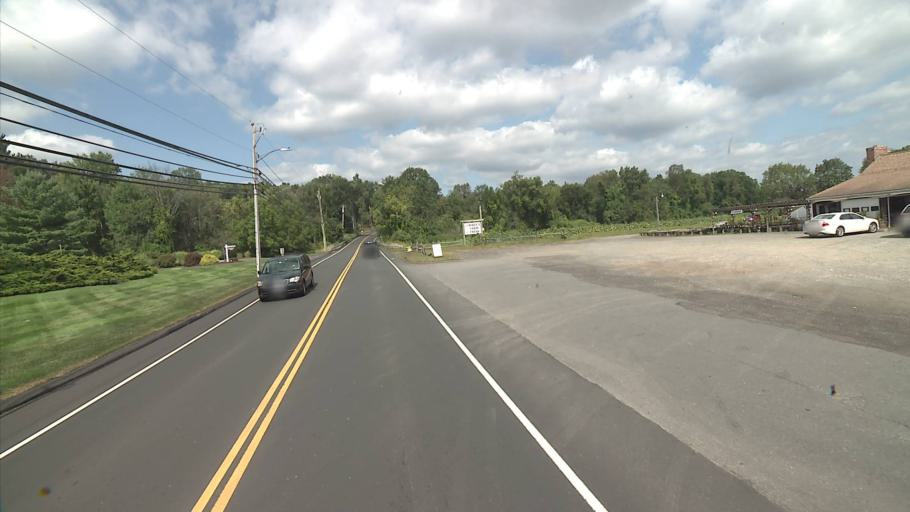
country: US
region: Connecticut
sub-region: Hartford County
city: Weatogue
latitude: 41.8305
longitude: -72.7722
